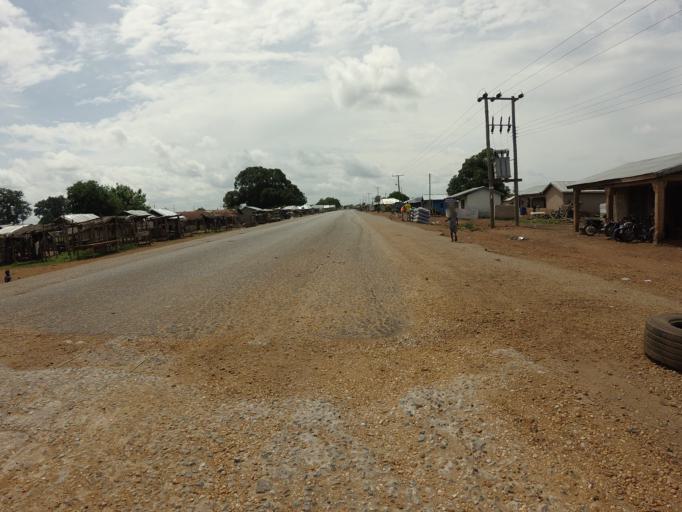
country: GH
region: Brong-Ahafo
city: Kintampo
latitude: 8.4474
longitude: -1.5649
